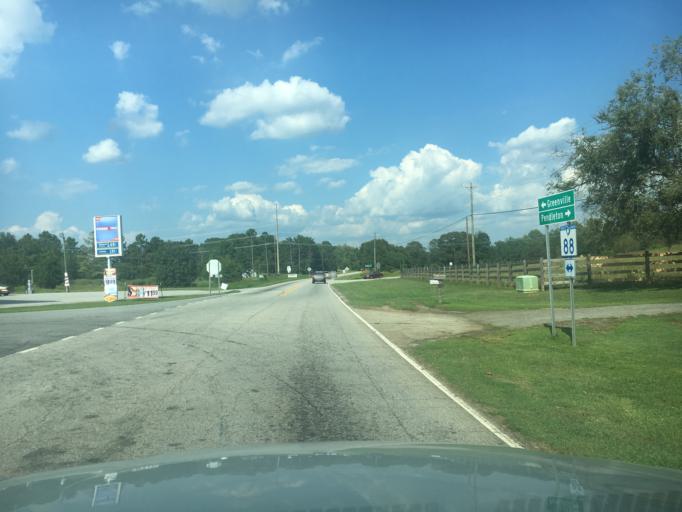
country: US
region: South Carolina
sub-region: Pickens County
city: Central
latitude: 34.6941
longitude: -82.7441
